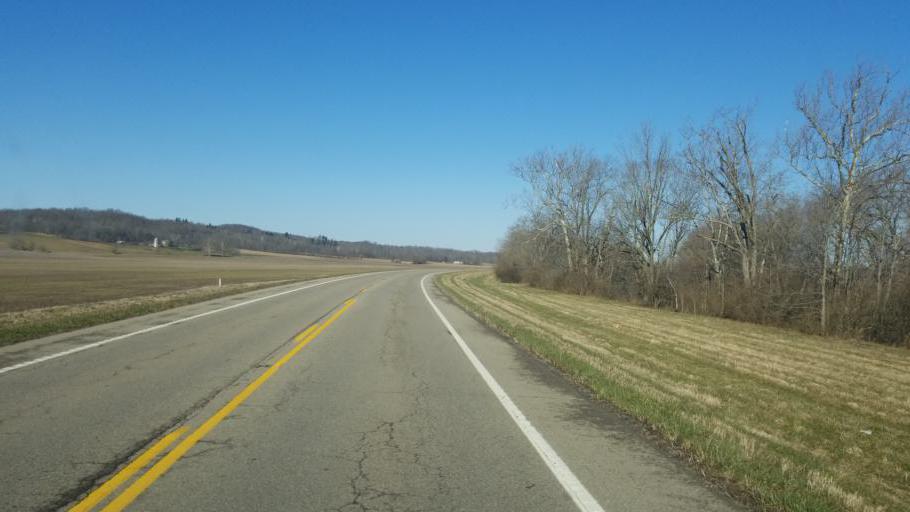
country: US
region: Ohio
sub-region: Highland County
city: Greenfield
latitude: 39.2210
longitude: -83.2955
